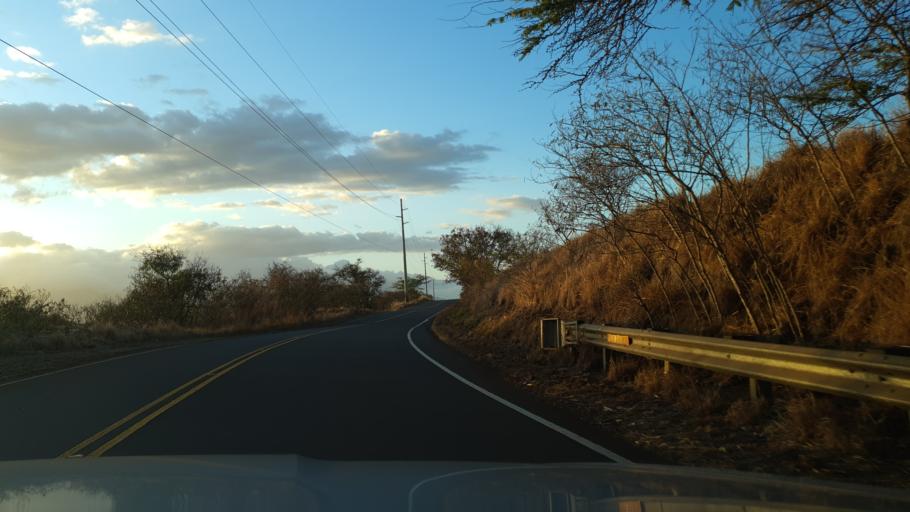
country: US
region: Hawaii
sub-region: Maui County
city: Pukalani
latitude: 20.8134
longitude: -156.3837
